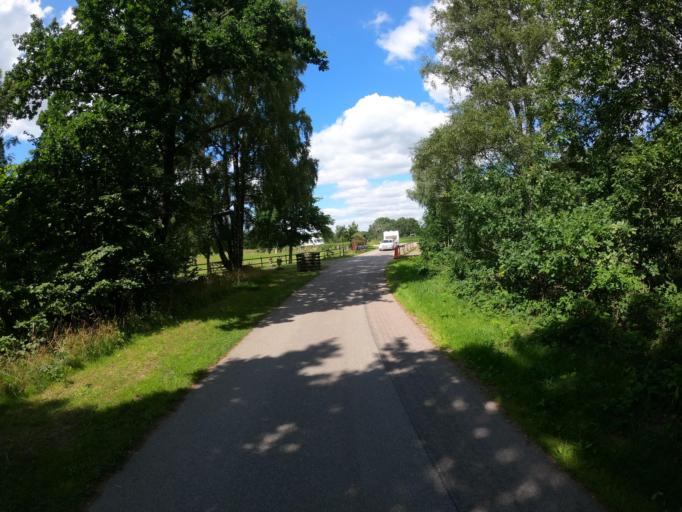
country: SE
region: Skane
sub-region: Lunds Kommun
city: Veberod
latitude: 55.5903
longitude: 13.4835
